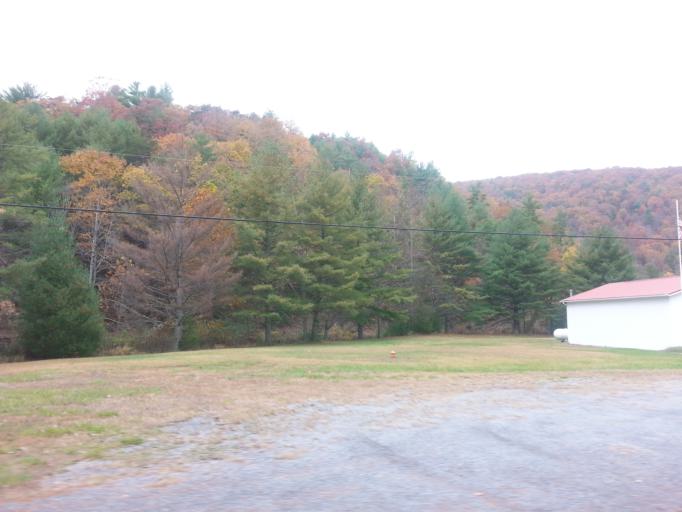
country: US
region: Virginia
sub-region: Bland County
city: Bland
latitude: 37.0720
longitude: -80.9609
